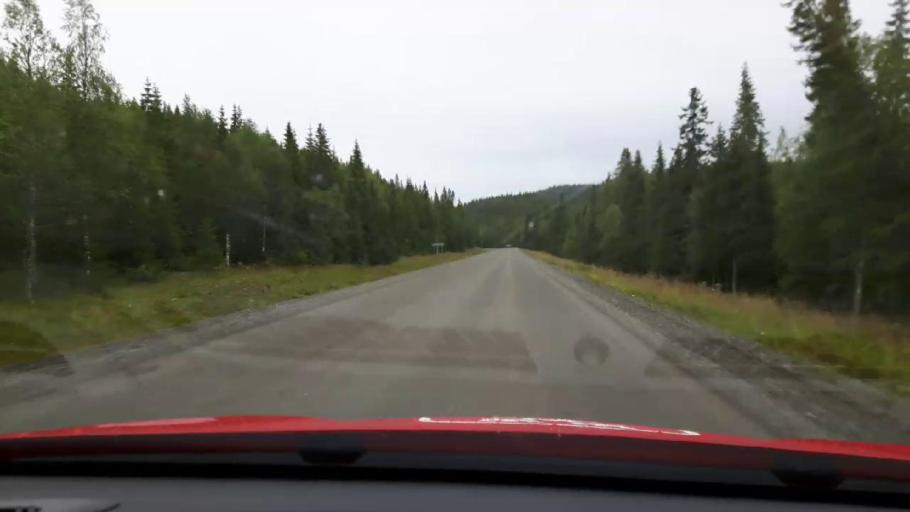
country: SE
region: Jaemtland
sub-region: Are Kommun
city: Are
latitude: 63.4260
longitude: 12.7399
